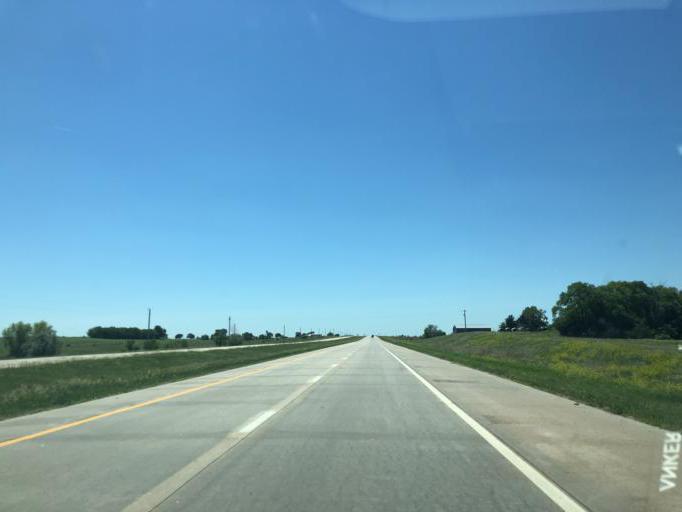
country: US
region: Kansas
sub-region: Republic County
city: Belleville
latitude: 39.9429
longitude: -97.6143
